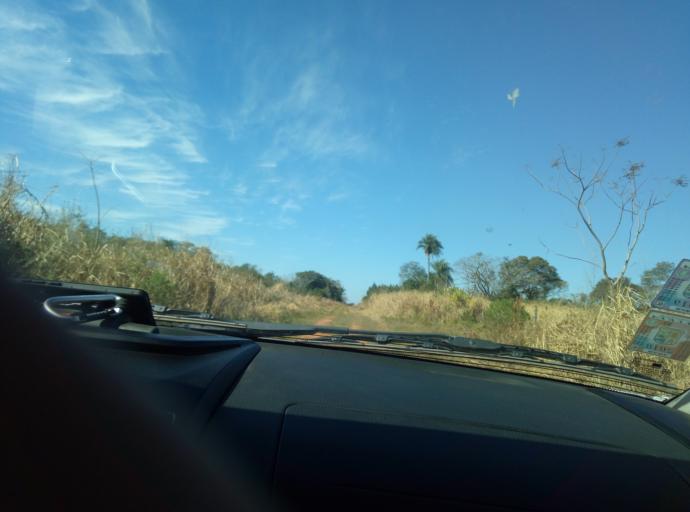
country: PY
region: Caaguazu
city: Carayao
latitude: -25.1757
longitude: -56.3065
